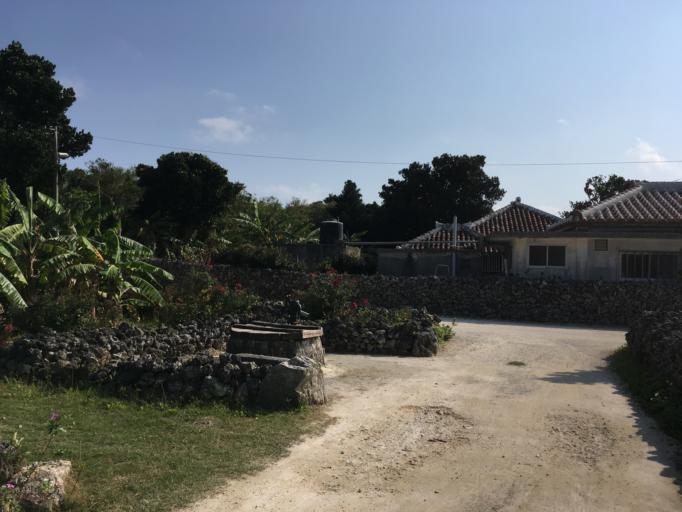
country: JP
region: Okinawa
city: Ishigaki
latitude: 24.3306
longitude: 124.0861
